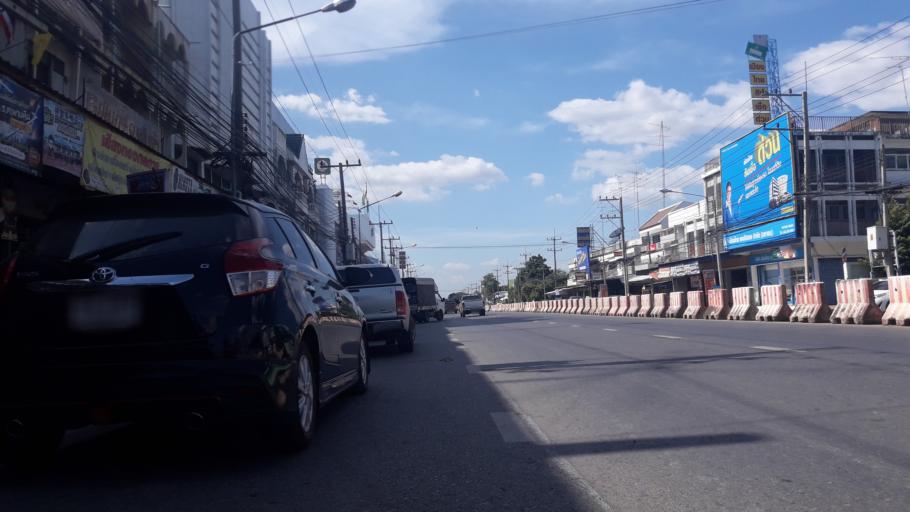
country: TH
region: Phichit
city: Thap Khlo
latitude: 16.1688
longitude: 100.5757
